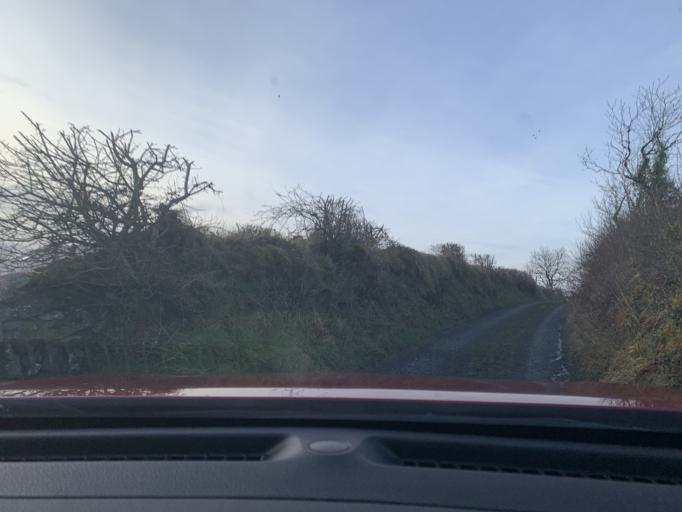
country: IE
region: Connaught
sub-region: Sligo
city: Strandhill
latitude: 54.1692
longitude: -8.6541
